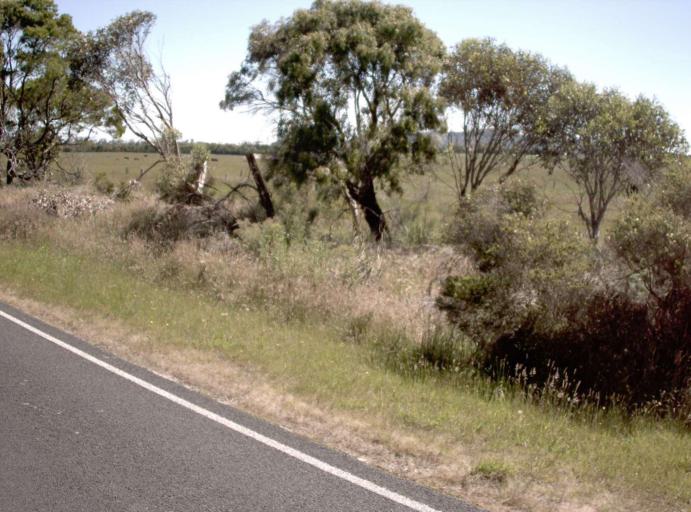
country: AU
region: Victoria
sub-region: Latrobe
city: Morwell
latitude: -38.6746
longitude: 146.1938
